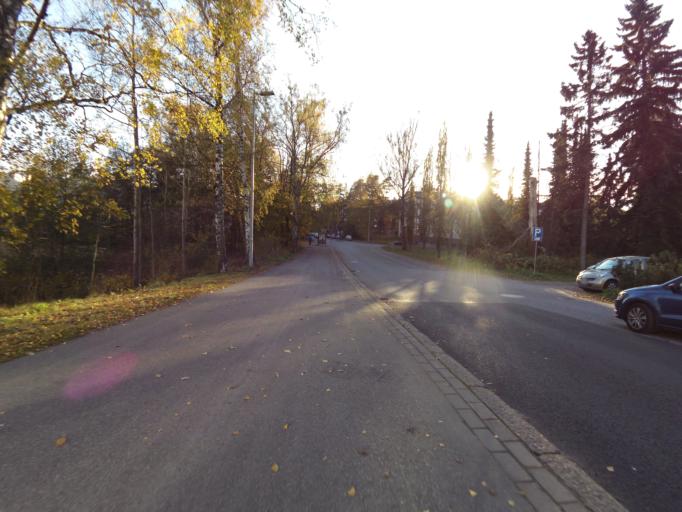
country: FI
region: Uusimaa
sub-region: Helsinki
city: Helsinki
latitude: 60.1890
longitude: 25.0164
